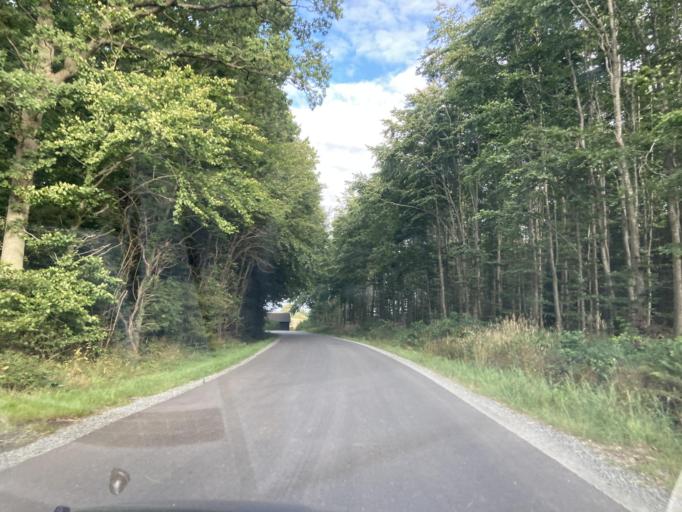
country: DK
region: South Denmark
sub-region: Kolding Kommune
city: Sonder Bjert
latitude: 55.4591
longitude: 9.6514
